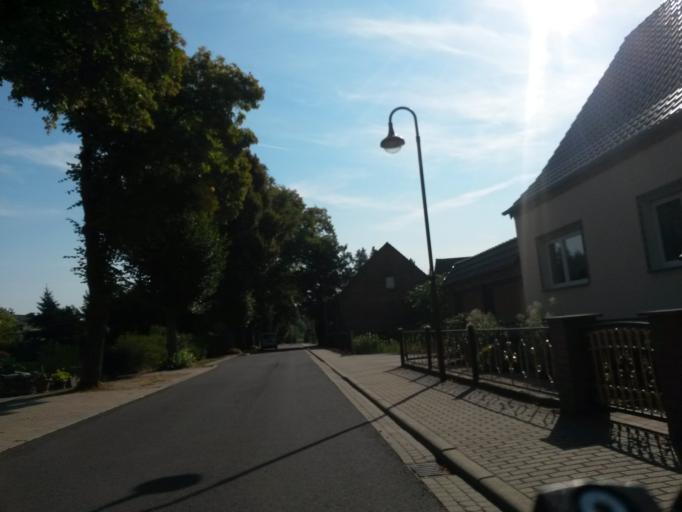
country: DE
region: Saxony-Anhalt
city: Nudersdorf
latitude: 51.9300
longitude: 12.5950
